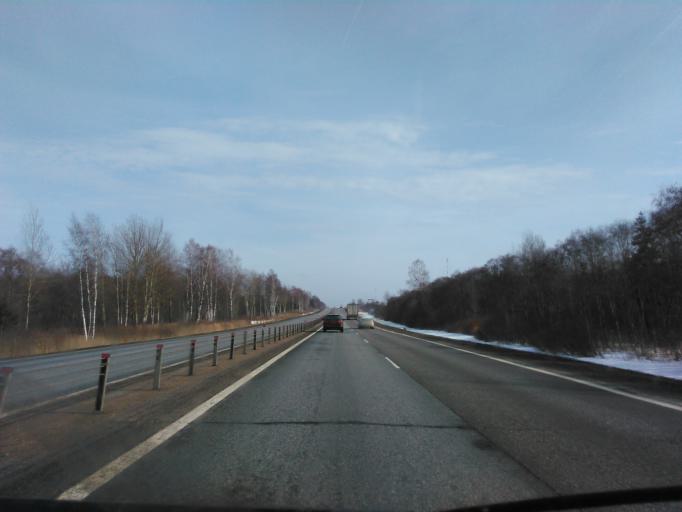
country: BY
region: Vitebsk
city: Dubrowna
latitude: 54.6878
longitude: 30.8602
